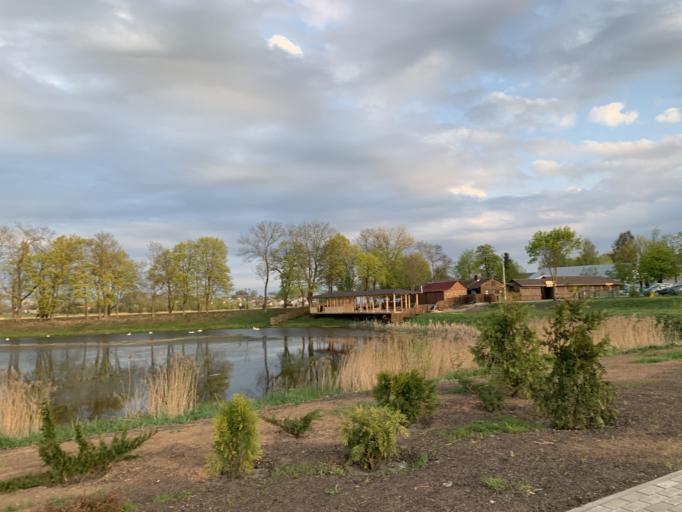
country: BY
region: Minsk
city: Nyasvizh
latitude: 53.2220
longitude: 26.6845
